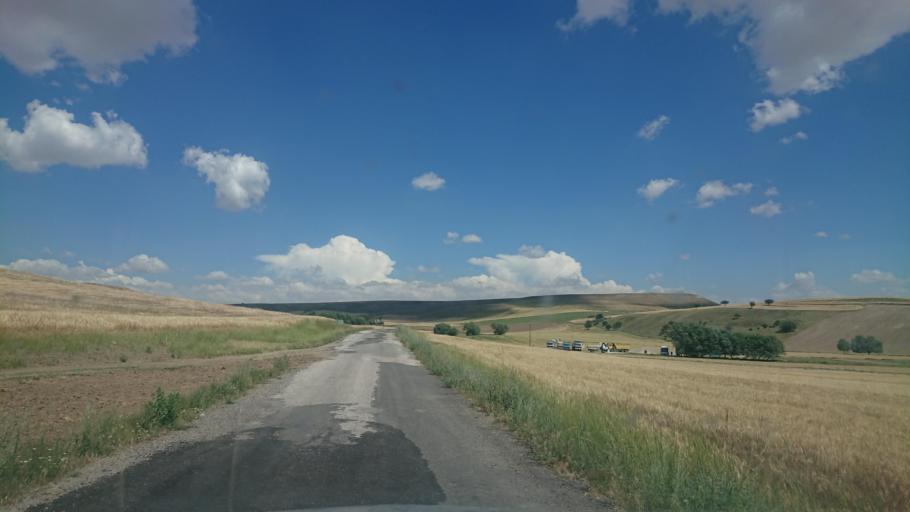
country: TR
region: Aksaray
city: Agacoren
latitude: 38.7999
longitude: 33.8220
